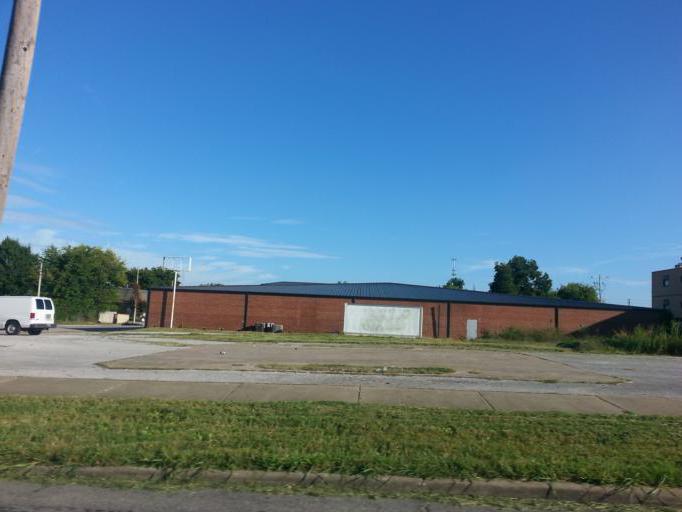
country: US
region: Alabama
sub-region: Lauderdale County
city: Florence
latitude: 34.8022
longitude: -87.6711
